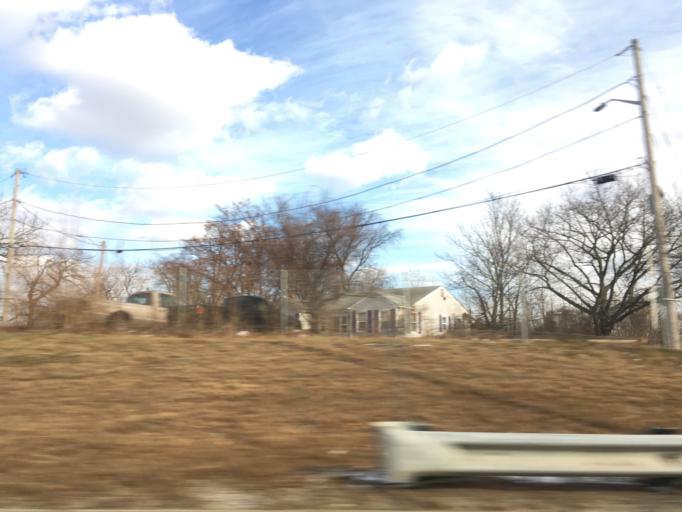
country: US
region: Rhode Island
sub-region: Providence County
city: Cranston
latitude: 41.7914
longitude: -71.4387
